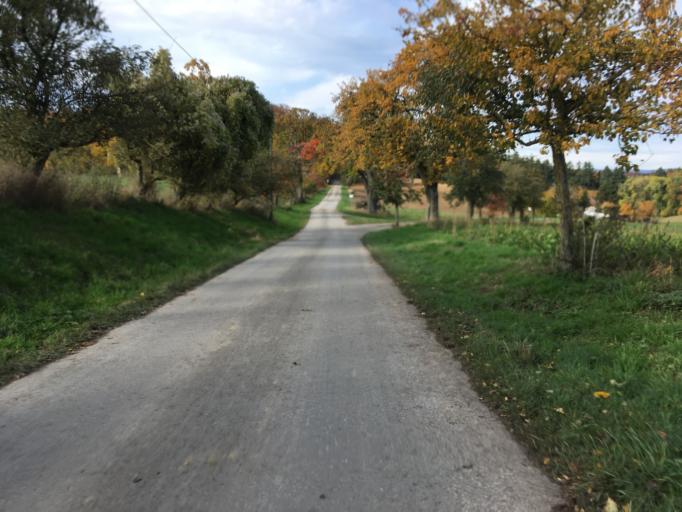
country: DE
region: Baden-Wuerttemberg
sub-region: Karlsruhe Region
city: Huffenhardt
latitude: 49.2719
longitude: 9.0290
